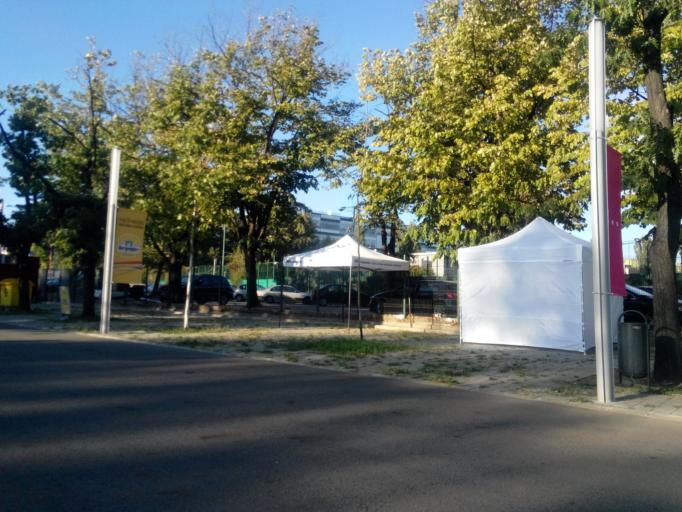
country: RO
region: Ilfov
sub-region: Comuna Fundeni-Dobroesti
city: Fundeni
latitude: 44.4389
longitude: 26.1511
